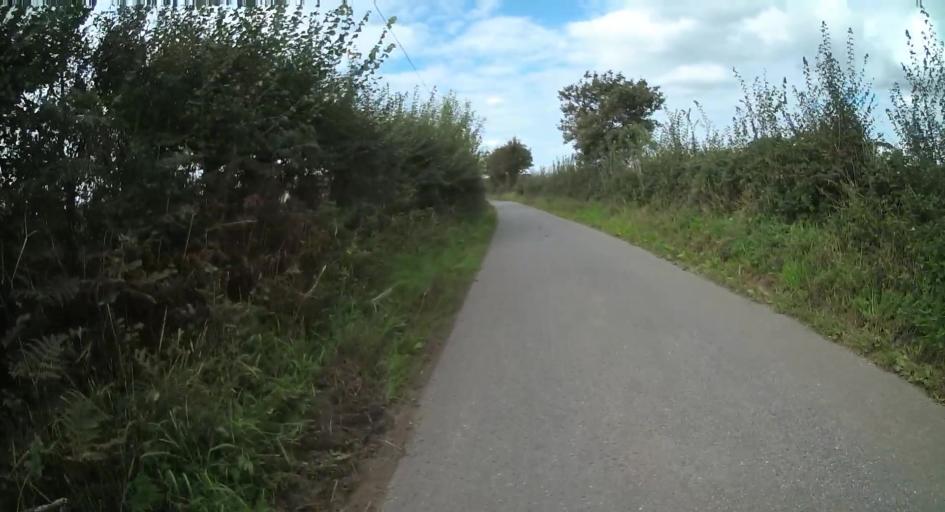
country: GB
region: England
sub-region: Isle of Wight
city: Niton
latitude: 50.6340
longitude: -1.2699
